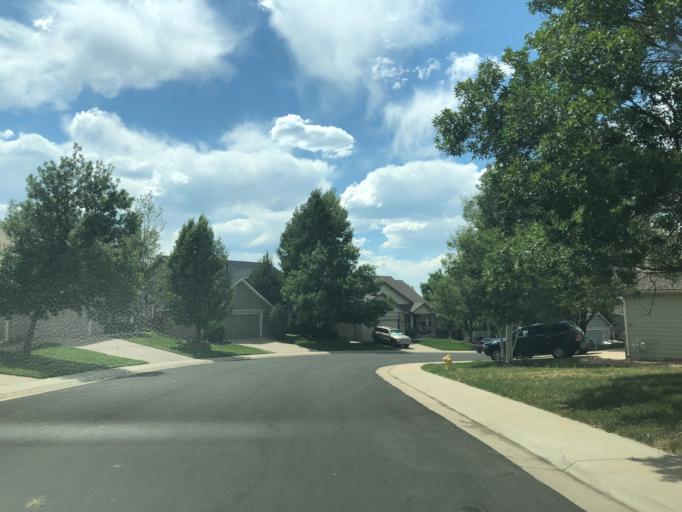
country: US
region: Colorado
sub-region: Arapahoe County
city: Dove Valley
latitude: 39.6209
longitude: -104.7698
